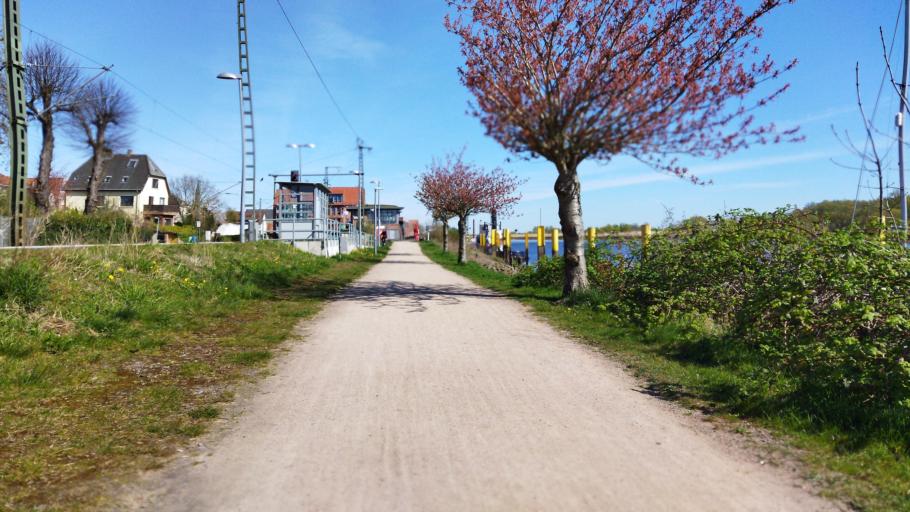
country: DE
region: Lower Saxony
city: Elsfleth
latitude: 53.2342
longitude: 8.4643
